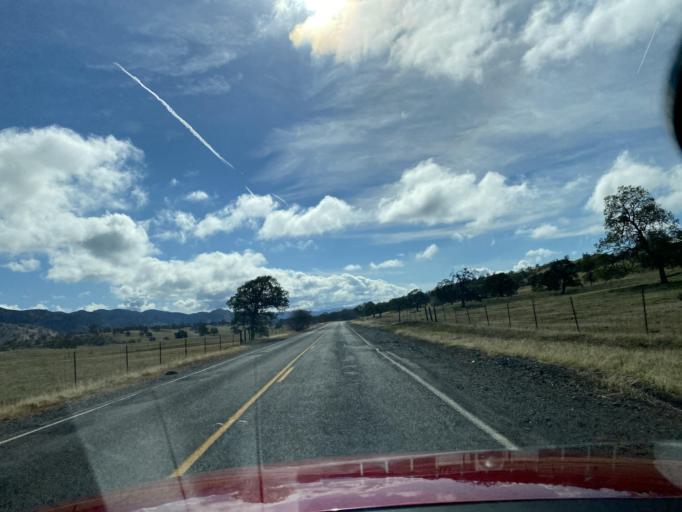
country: US
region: California
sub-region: Glenn County
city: Willows
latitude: 39.4978
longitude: -122.5225
